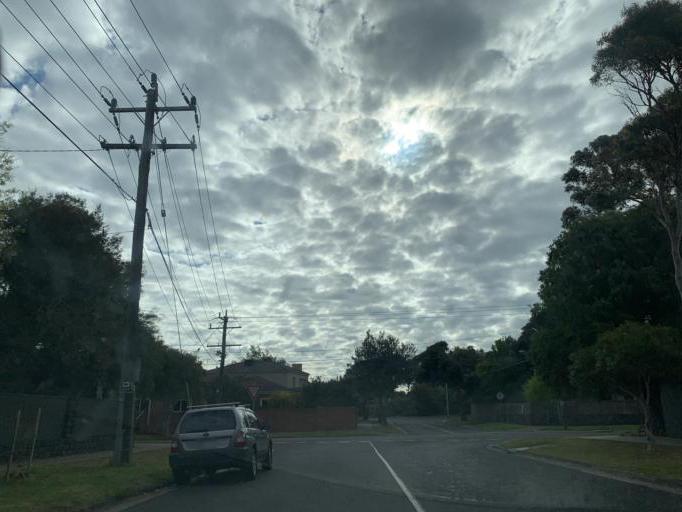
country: AU
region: Victoria
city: Beaumaris
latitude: -37.9863
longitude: 145.0286
